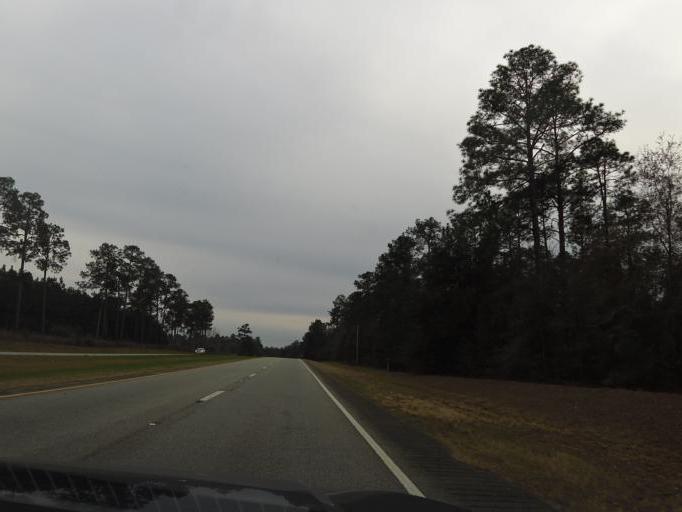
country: US
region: Florida
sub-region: Jefferson County
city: Monticello
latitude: 30.6830
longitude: -83.8871
